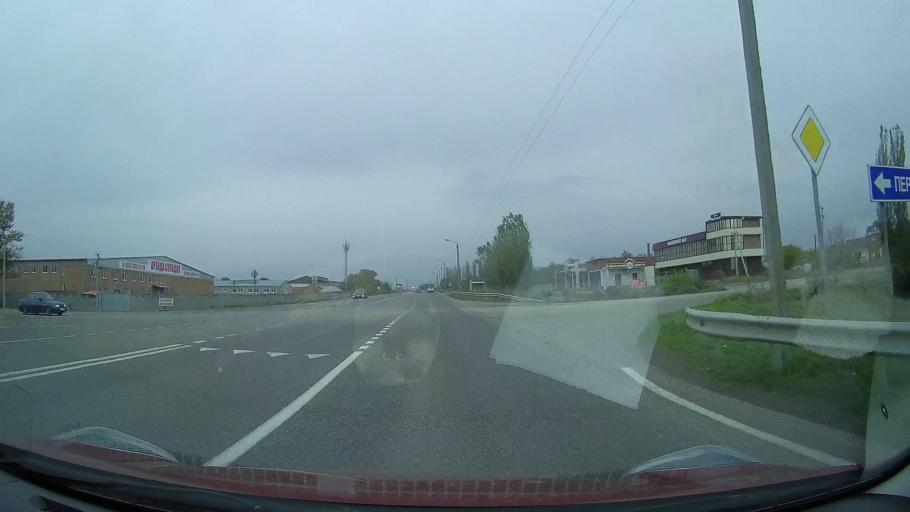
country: RU
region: Stavropol'skiy
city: Levokumka
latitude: 44.2520
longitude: 43.1253
